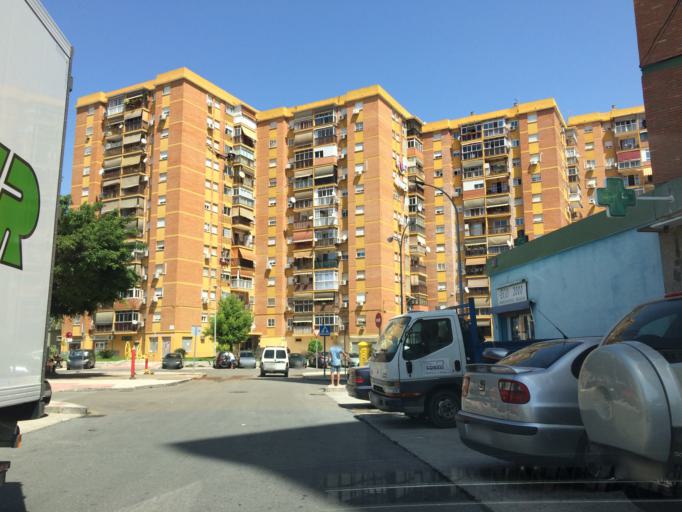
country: ES
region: Andalusia
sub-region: Provincia de Malaga
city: Malaga
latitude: 36.7041
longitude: -4.4561
